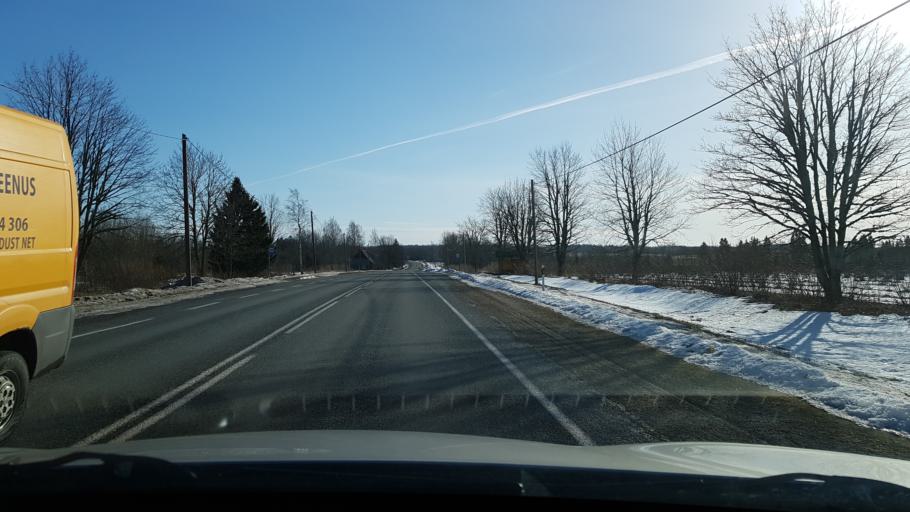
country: EE
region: Viljandimaa
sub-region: Suure-Jaani vald
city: Suure-Jaani
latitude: 58.5559
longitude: 25.4460
